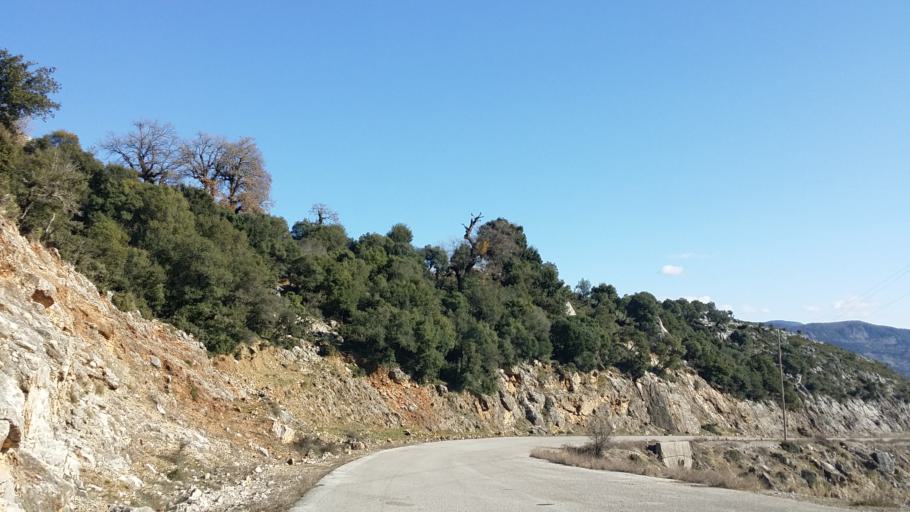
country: GR
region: Central Greece
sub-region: Nomos Evrytanias
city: Kerasochori
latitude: 38.9650
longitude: 21.4718
